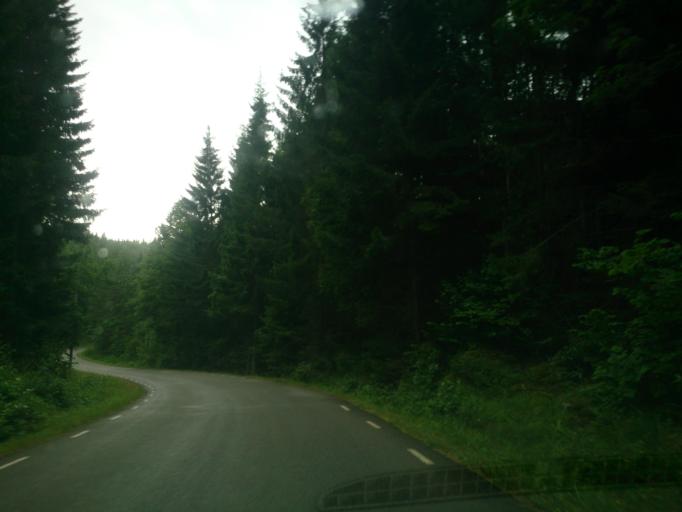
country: SE
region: OEstergoetland
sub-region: Atvidabergs Kommun
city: Atvidaberg
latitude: 58.2774
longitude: 16.1344
